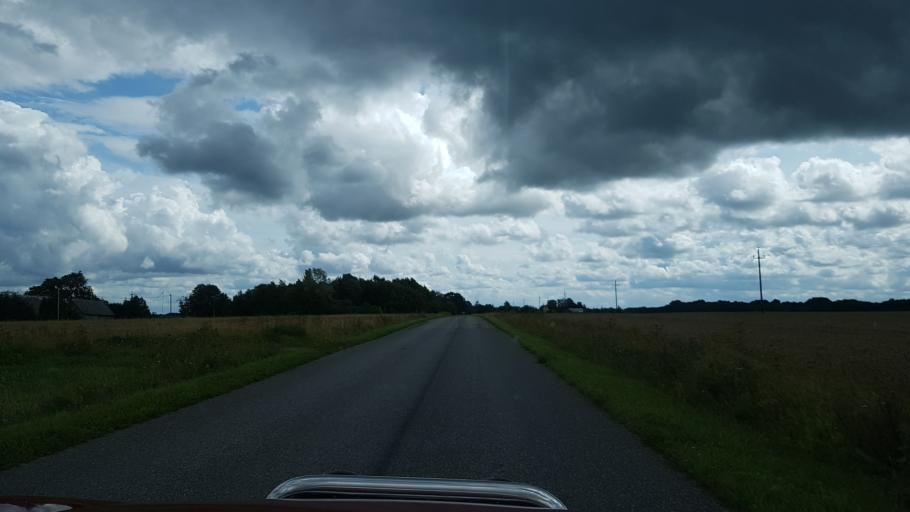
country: EE
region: Laeaene
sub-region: Lihula vald
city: Lihula
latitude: 58.7148
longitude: 23.9985
